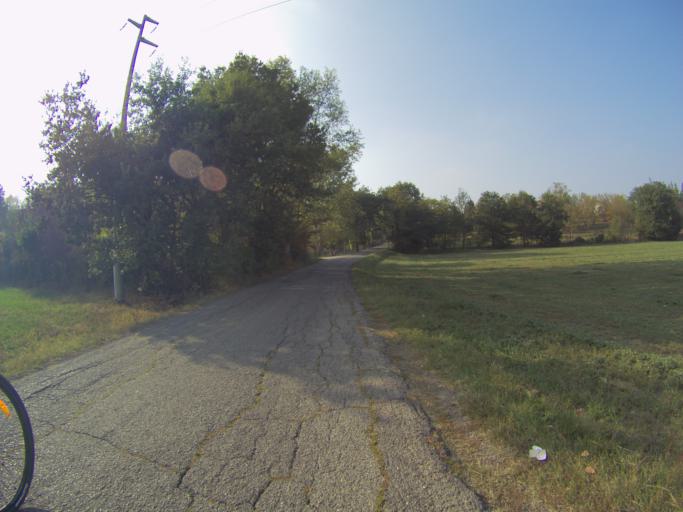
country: IT
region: Emilia-Romagna
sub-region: Provincia di Reggio Emilia
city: Forche
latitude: 44.6520
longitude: 10.5691
